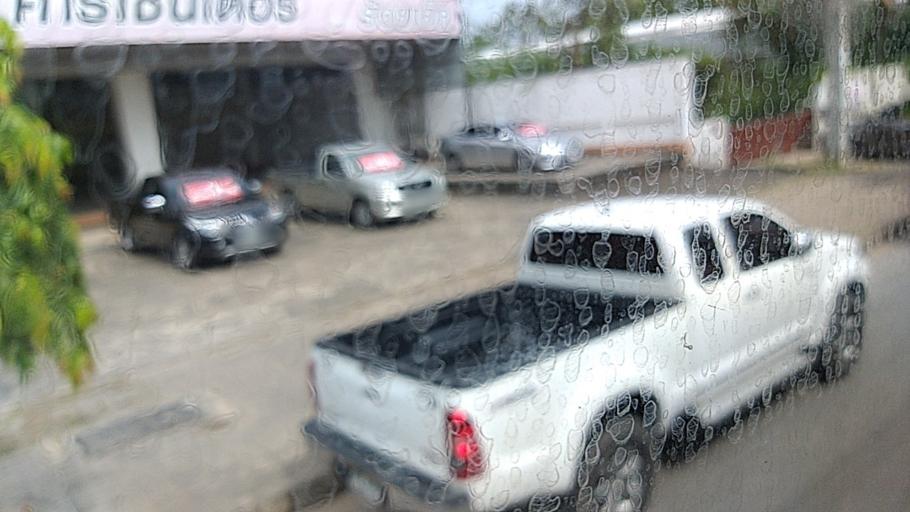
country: TH
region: Roi Et
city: Roi Et
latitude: 16.0596
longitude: 103.6295
